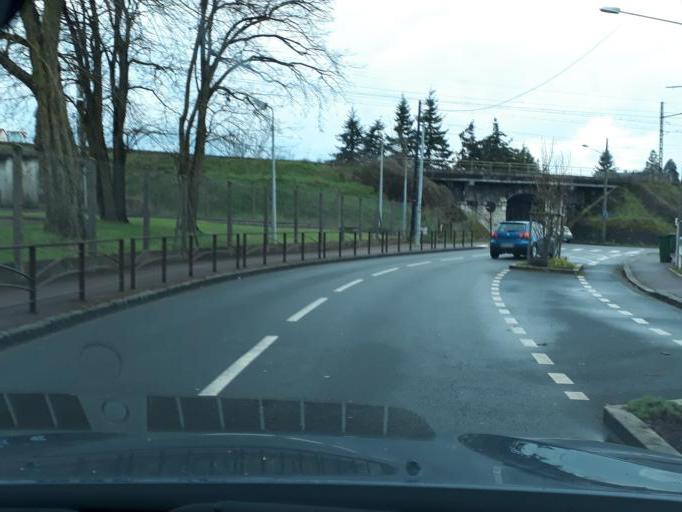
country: FR
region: Centre
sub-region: Departement du Loiret
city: Saint-Jean-de-la-Ruelle
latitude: 47.9133
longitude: 1.8821
